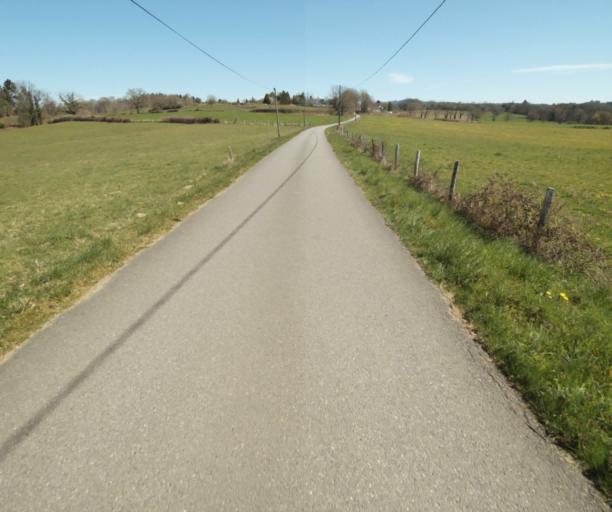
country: FR
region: Limousin
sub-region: Departement de la Correze
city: Chamboulive
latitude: 45.4617
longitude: 1.7145
